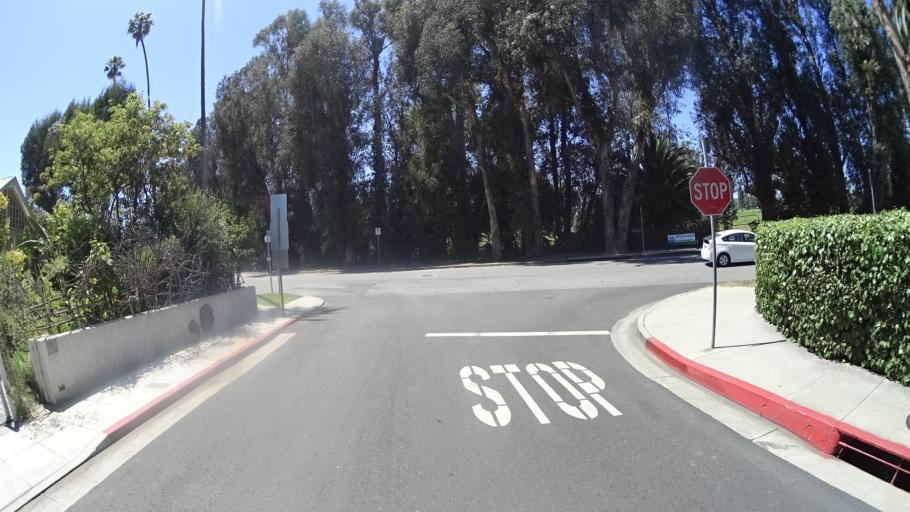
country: US
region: California
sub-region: Los Angeles County
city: Santa Monica
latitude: 34.0463
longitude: -118.4778
